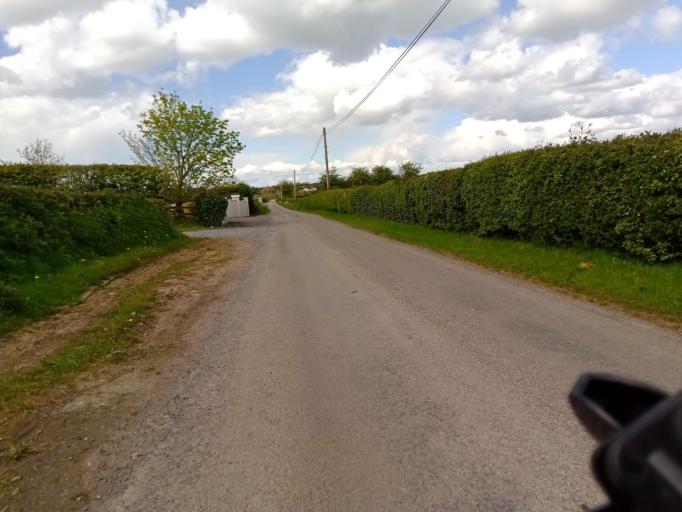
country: IE
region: Leinster
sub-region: Kilkenny
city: Thomastown
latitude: 52.5905
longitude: -7.1463
